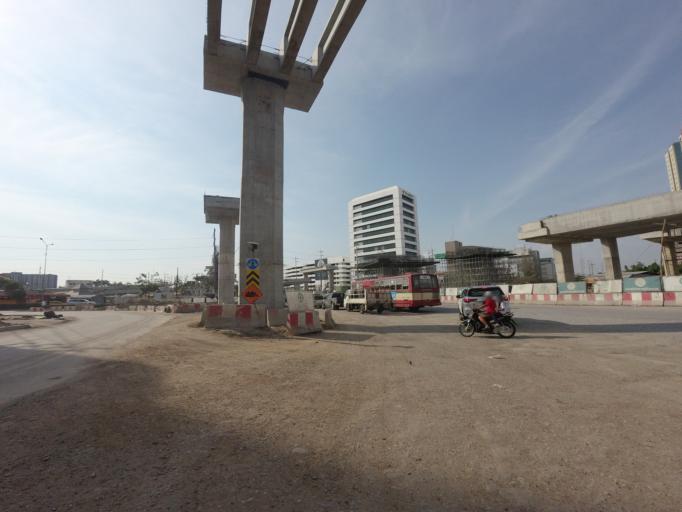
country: TH
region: Bangkok
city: Bang Kapi
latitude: 13.7514
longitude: 100.6457
